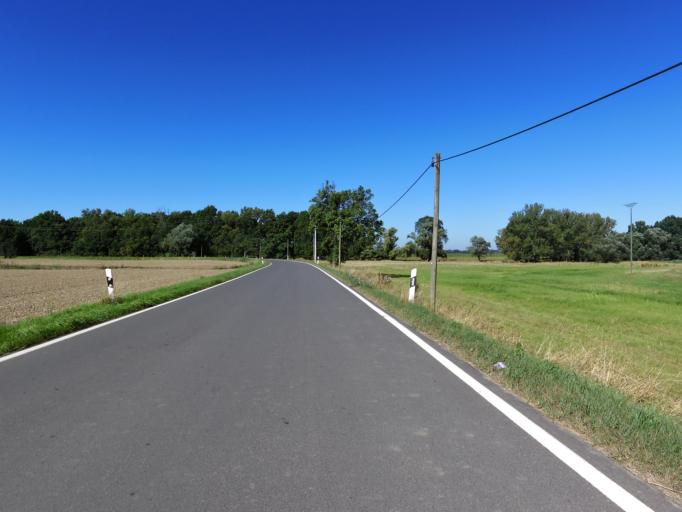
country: DE
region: Saxony
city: Elsnig
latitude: 51.6304
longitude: 12.9245
